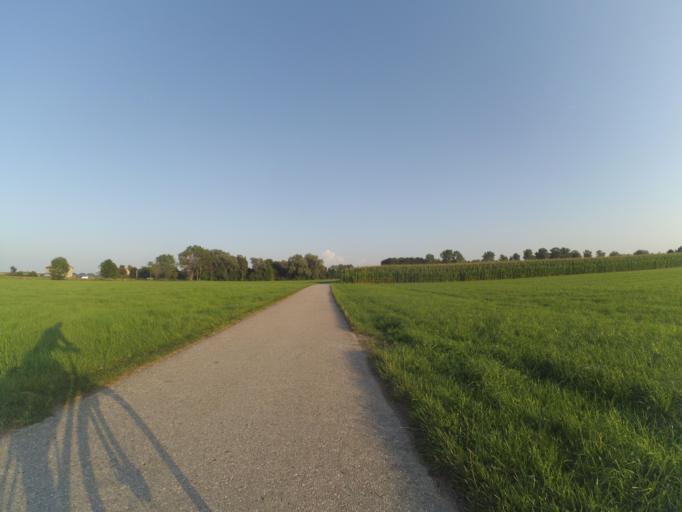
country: DE
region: Bavaria
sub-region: Swabia
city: Jengen
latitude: 48.0091
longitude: 10.7201
